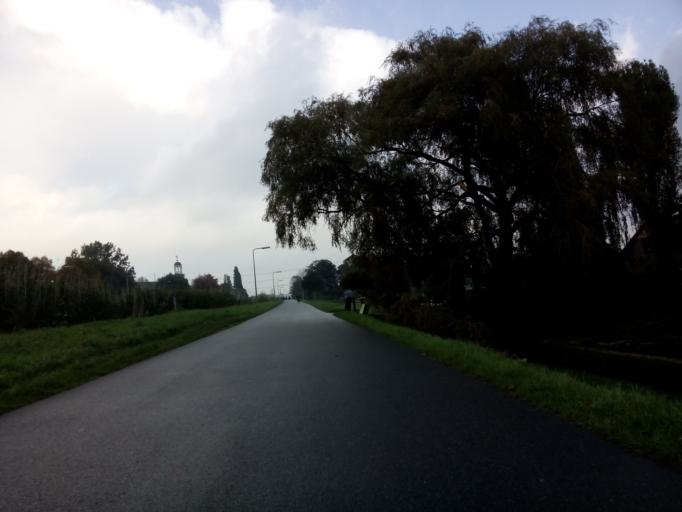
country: NL
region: South Holland
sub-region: Gemeente Delft
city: Delft
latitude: 51.9847
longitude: 4.3203
